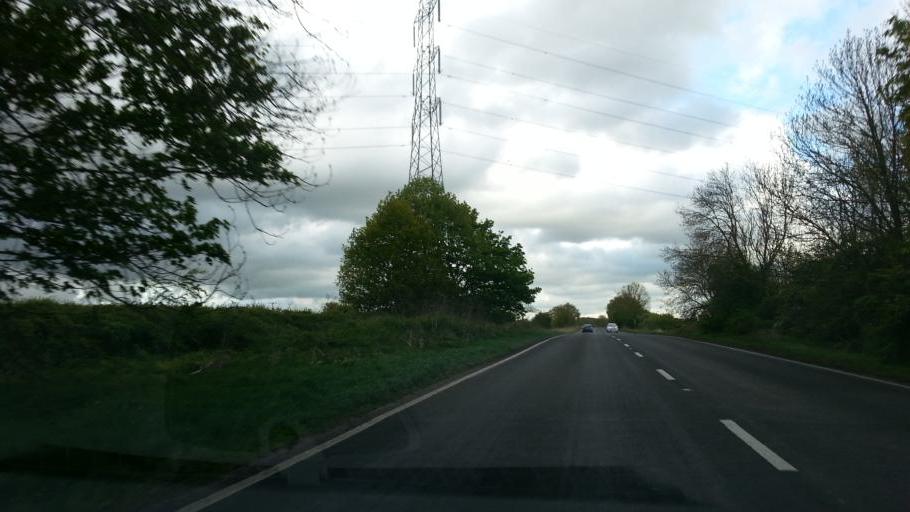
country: GB
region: England
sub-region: Nottinghamshire
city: Farndon
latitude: 53.1234
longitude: -0.8761
